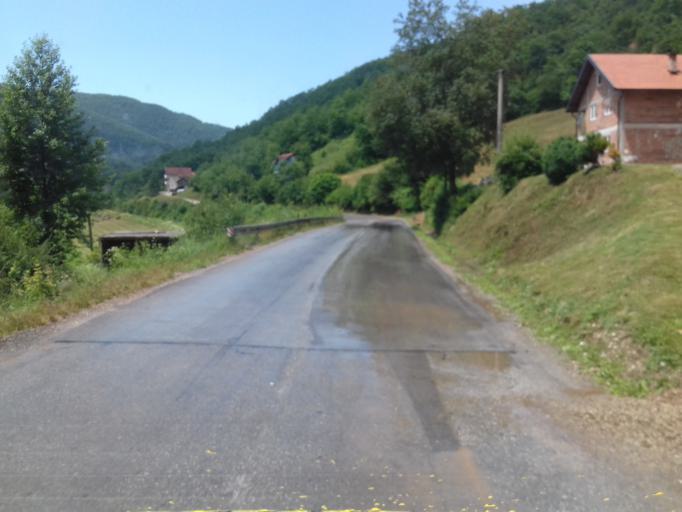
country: BA
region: Federation of Bosnia and Herzegovina
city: Visoko
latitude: 43.9542
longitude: 18.1376
